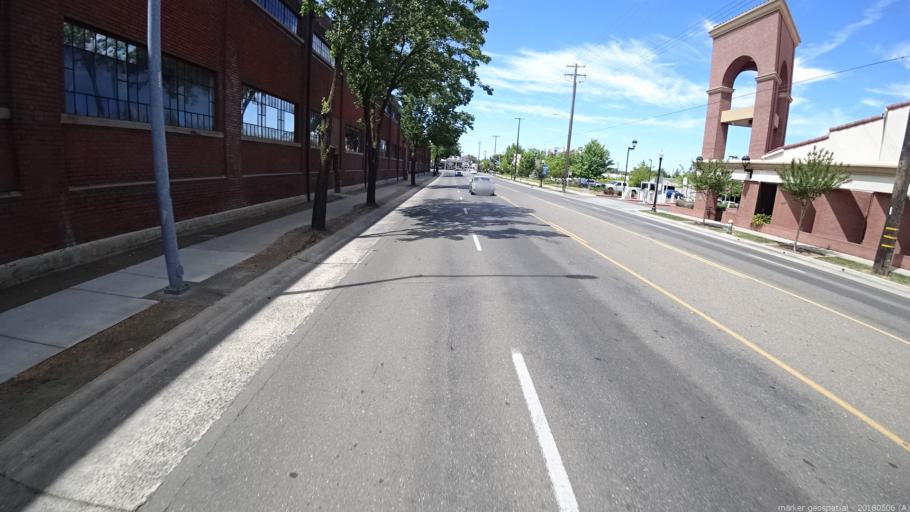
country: US
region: California
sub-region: Sacramento County
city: Sacramento
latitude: 38.5651
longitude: -121.4671
